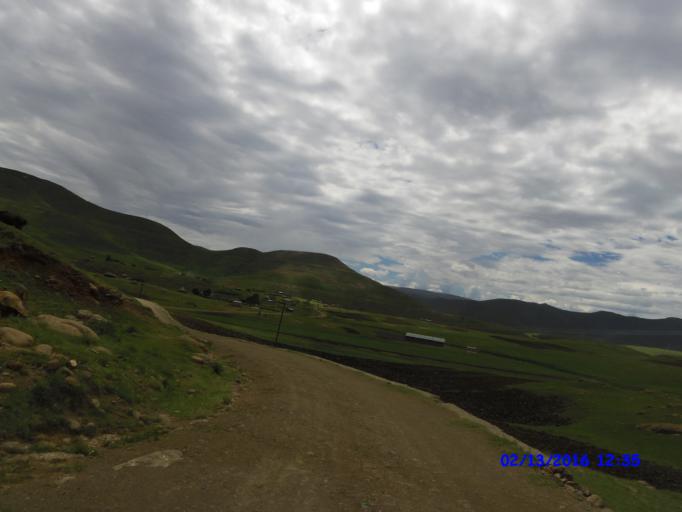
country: LS
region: Maseru
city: Nako
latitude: -29.8431
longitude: 28.0242
